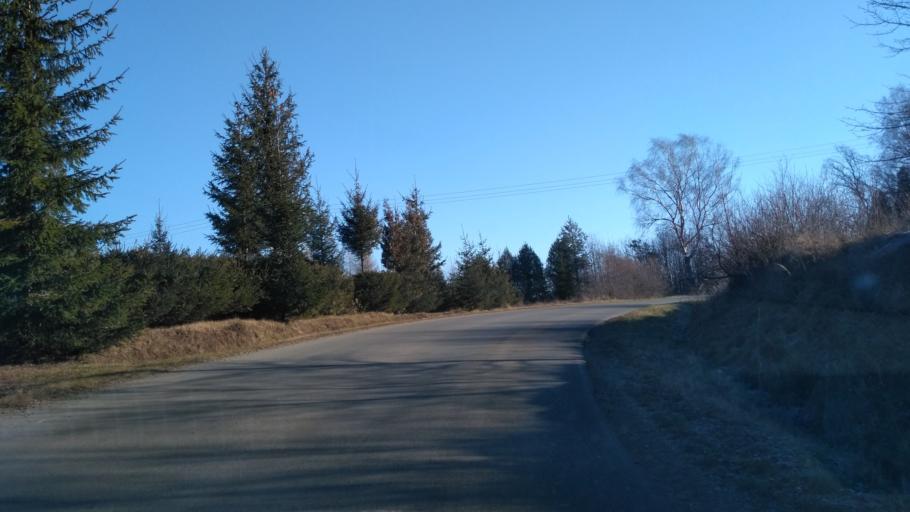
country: PL
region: Subcarpathian Voivodeship
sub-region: Powiat krosnienski
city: Rymanow
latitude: 49.5718
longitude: 21.8783
